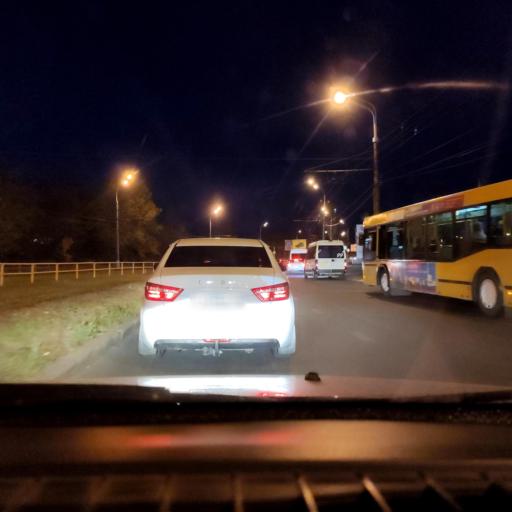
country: RU
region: Samara
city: Tol'yatti
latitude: 53.5070
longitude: 49.2545
